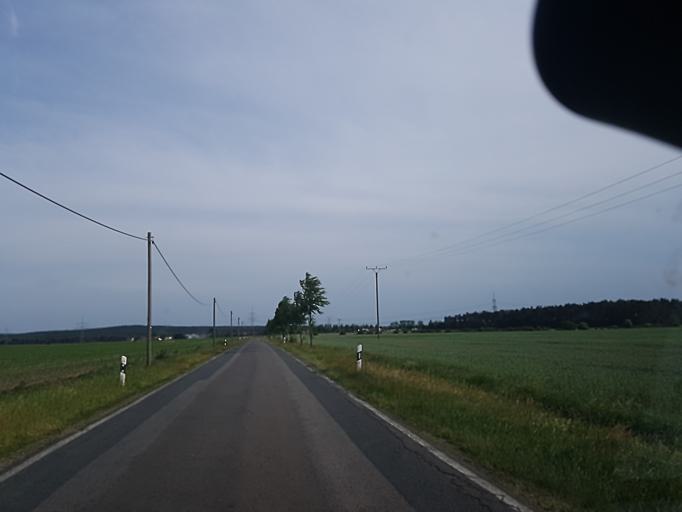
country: DE
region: Saxony-Anhalt
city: Jessen
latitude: 51.8312
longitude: 12.9454
